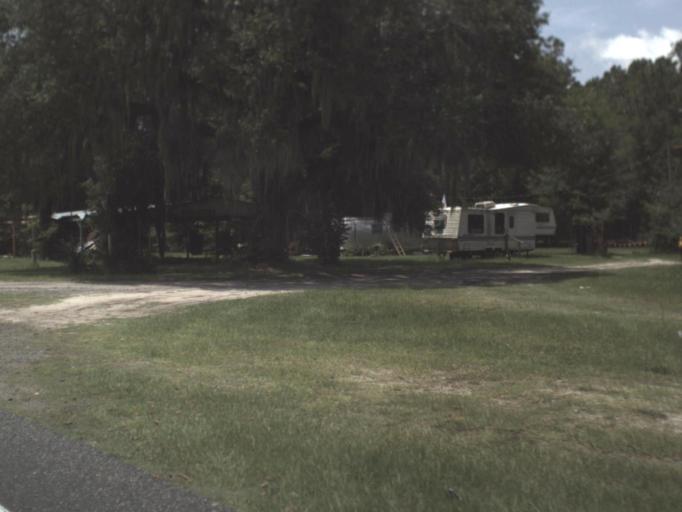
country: US
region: Florida
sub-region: Taylor County
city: Perry
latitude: 30.0486
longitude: -83.5510
